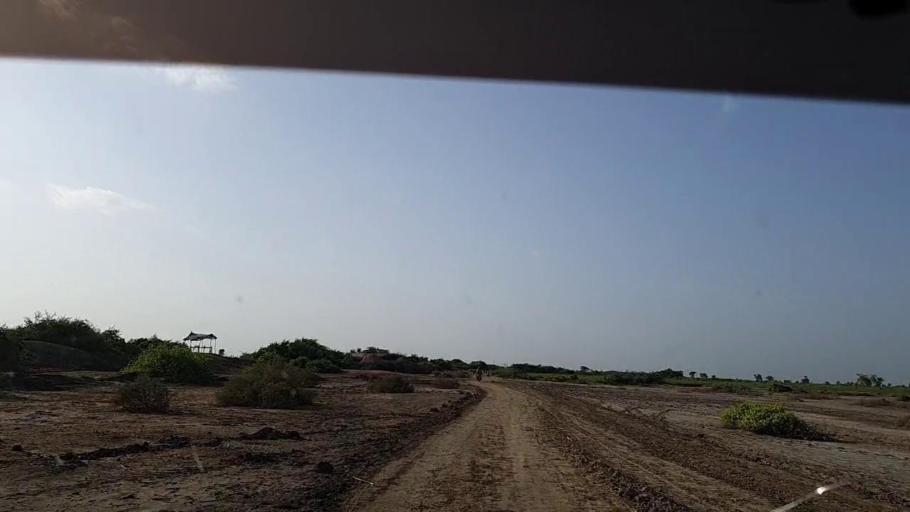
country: PK
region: Sindh
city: Badin
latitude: 24.5718
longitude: 68.8769
